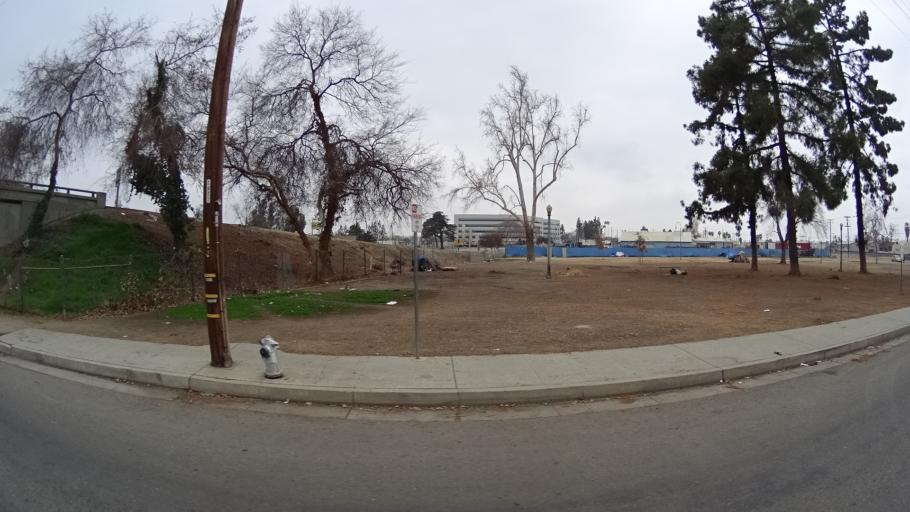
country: US
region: California
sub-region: Kern County
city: Bakersfield
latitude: 35.3830
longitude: -119.0106
